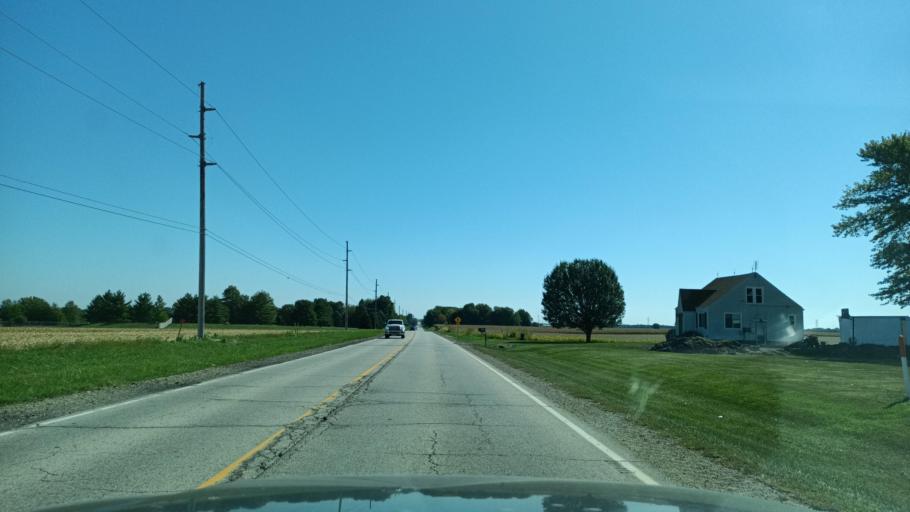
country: US
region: Illinois
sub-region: Peoria County
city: Dunlap
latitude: 40.7865
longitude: -89.7316
